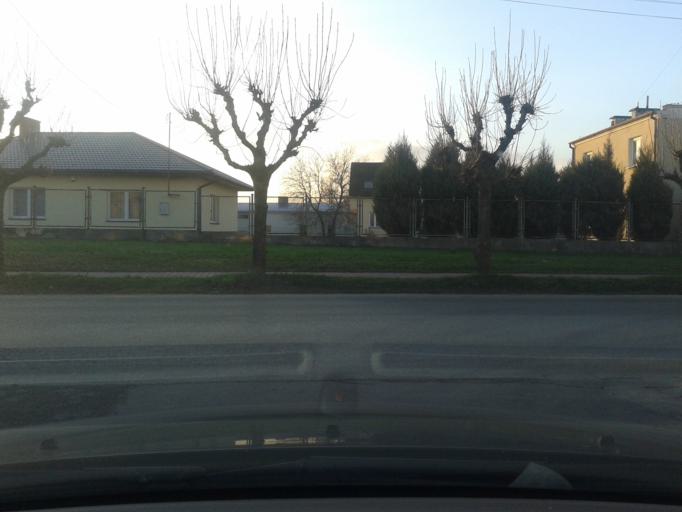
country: PL
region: Lublin Voivodeship
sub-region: Powiat opolski
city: Opole Lubelskie
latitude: 51.1405
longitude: 21.9780
